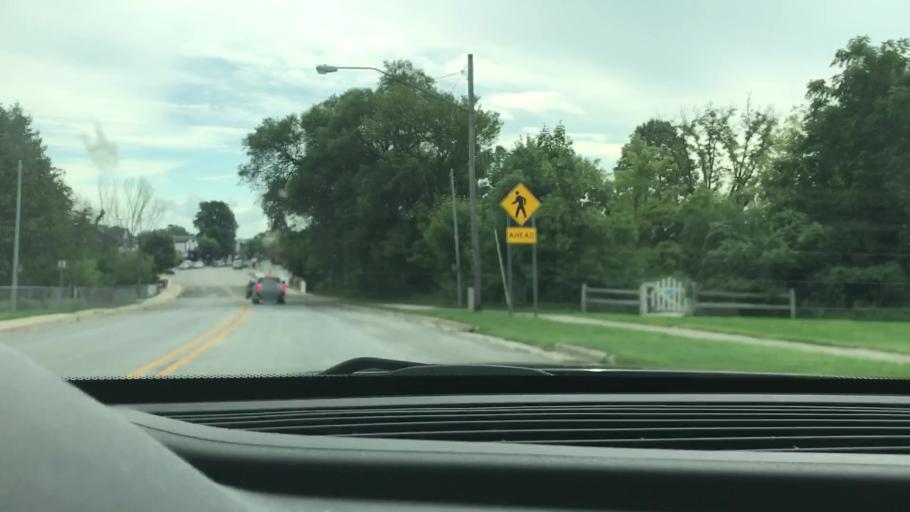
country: US
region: Michigan
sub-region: Antrim County
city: Bellaire
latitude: 44.9796
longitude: -85.2103
